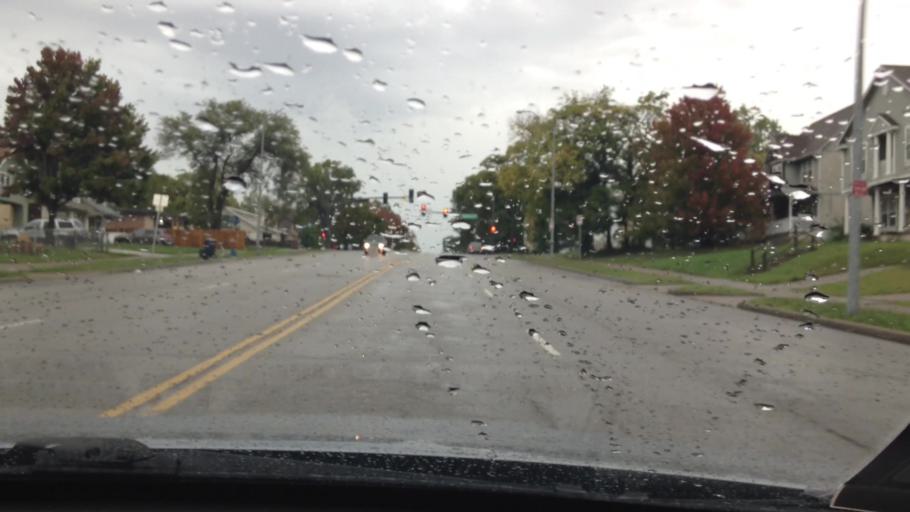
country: US
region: Missouri
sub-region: Jackson County
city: Kansas City
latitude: 39.0549
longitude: -94.5674
